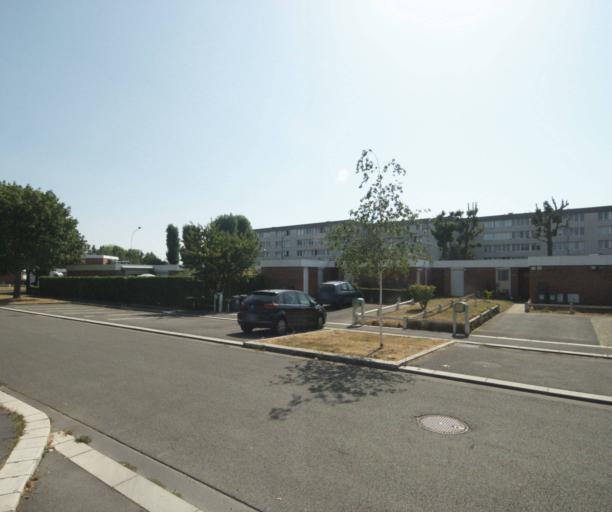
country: FR
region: Nord-Pas-de-Calais
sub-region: Departement du Nord
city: Wattrelos
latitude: 50.7041
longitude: 3.2385
